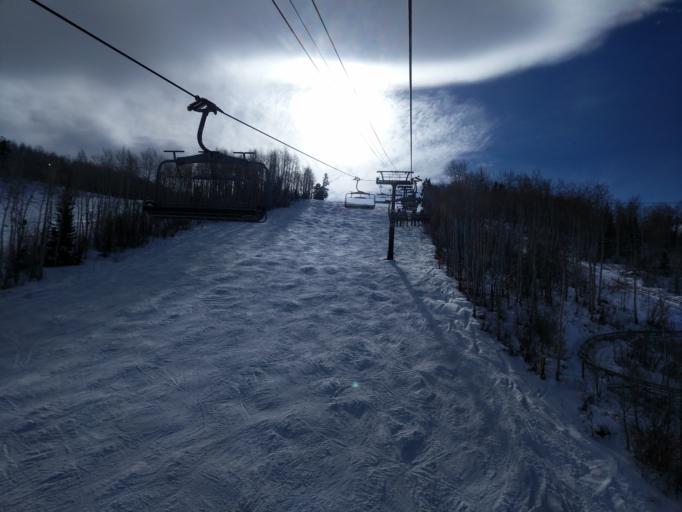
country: US
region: Utah
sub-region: Summit County
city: Park City
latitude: 40.6465
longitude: -111.5081
